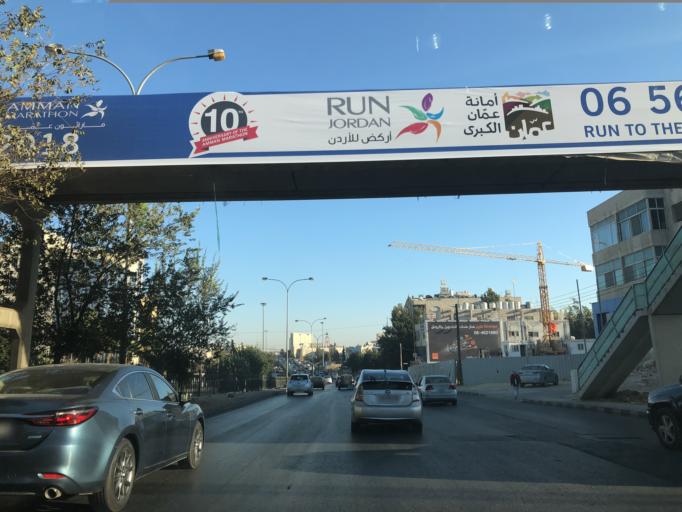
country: JO
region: Amman
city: Wadi as Sir
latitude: 31.9606
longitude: 35.8451
